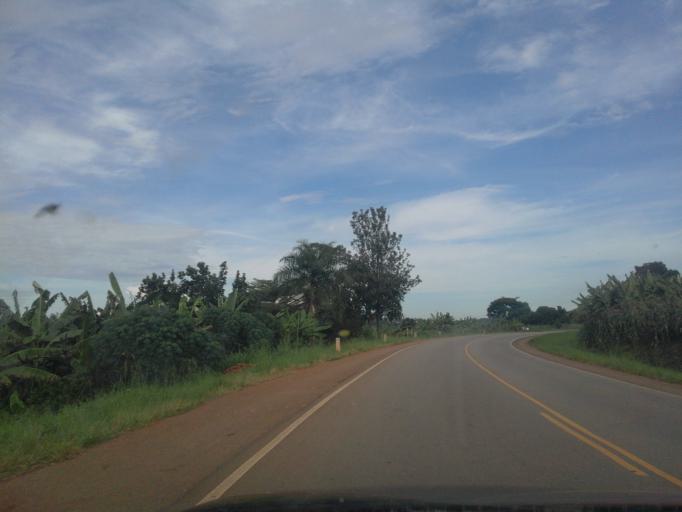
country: UG
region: Central Region
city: Masaka
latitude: -0.3428
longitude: 31.6292
